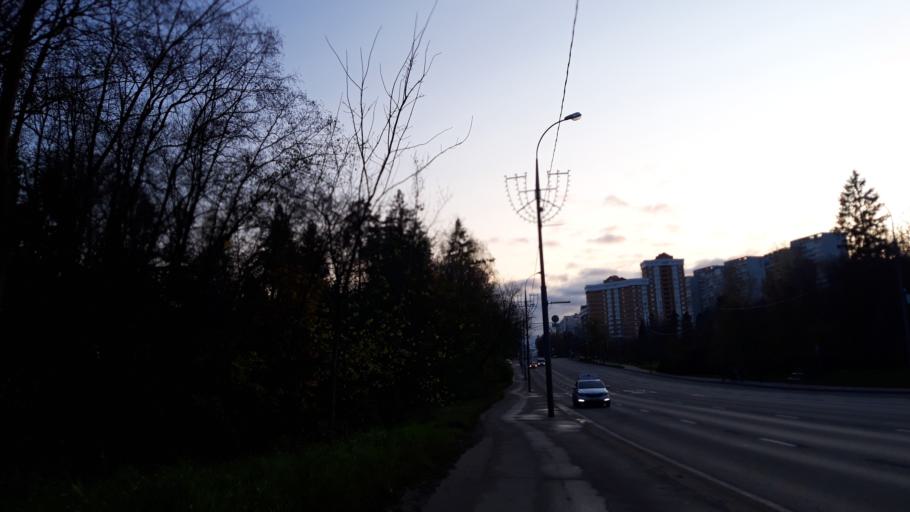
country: RU
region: Moscow
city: Zelenograd
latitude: 55.9909
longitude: 37.1860
